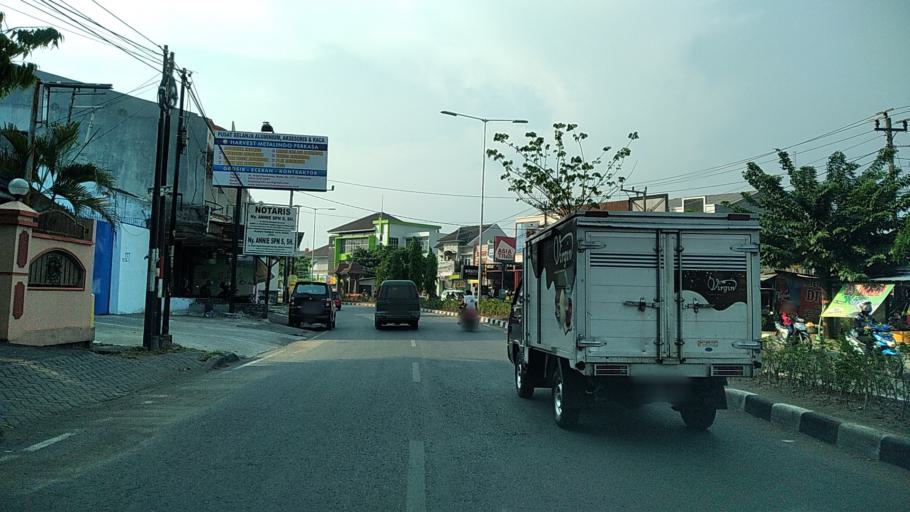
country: ID
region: Central Java
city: Semarang
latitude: -6.9937
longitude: 110.4601
